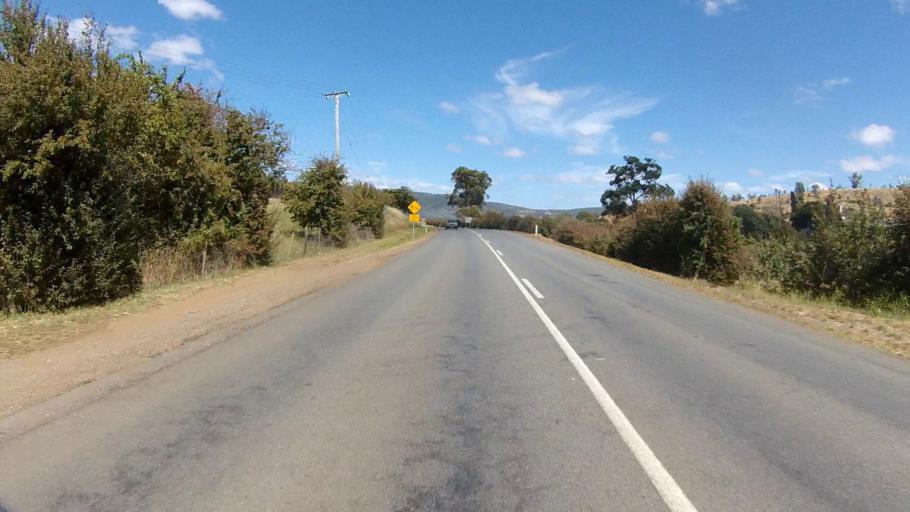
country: AU
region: Tasmania
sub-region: Clarence
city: Cambridge
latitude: -42.7392
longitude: 147.4270
